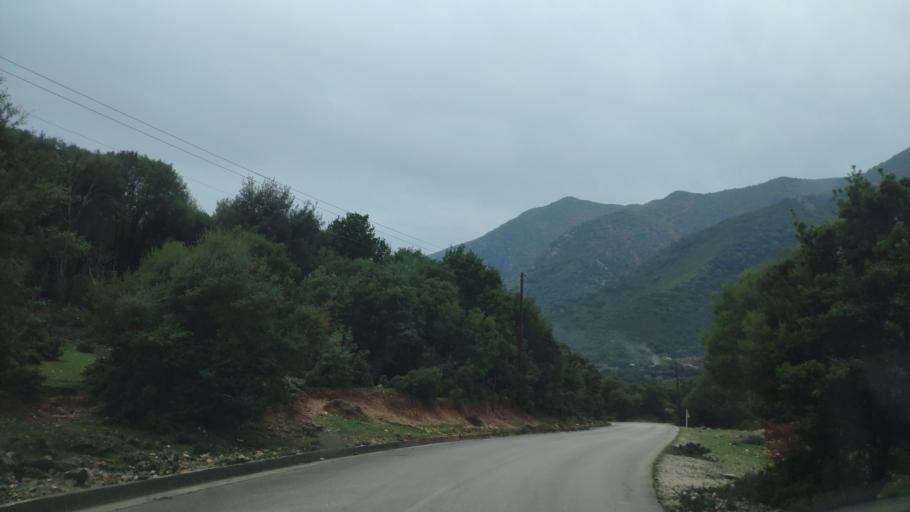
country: GR
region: Epirus
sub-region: Nomos Thesprotias
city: Paramythia
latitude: 39.3960
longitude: 20.6244
